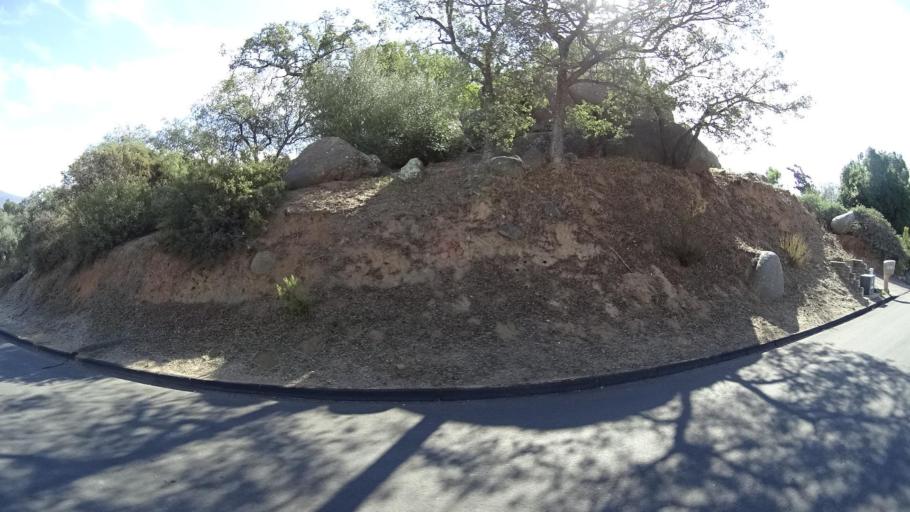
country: US
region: California
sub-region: San Diego County
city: Alpine
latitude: 32.8146
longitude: -116.7740
